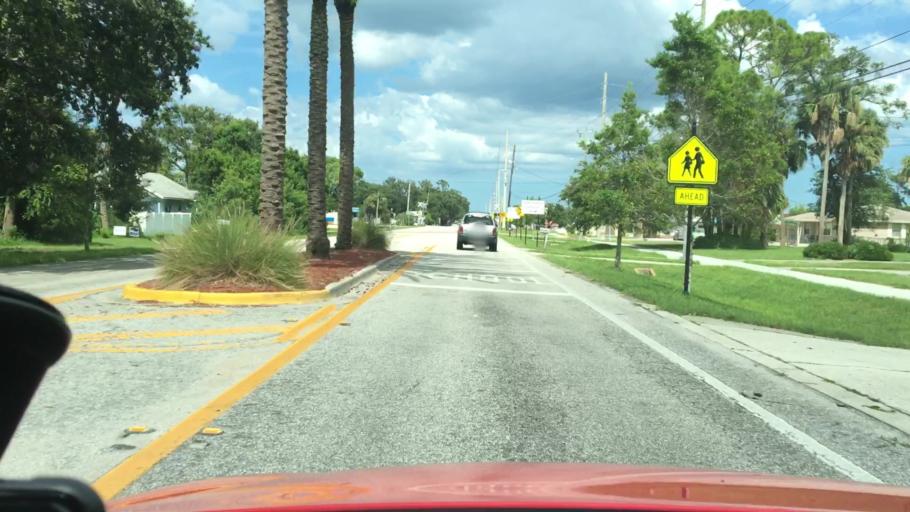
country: US
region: Florida
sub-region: Volusia County
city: South Daytona
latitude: 29.1726
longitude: -81.0094
